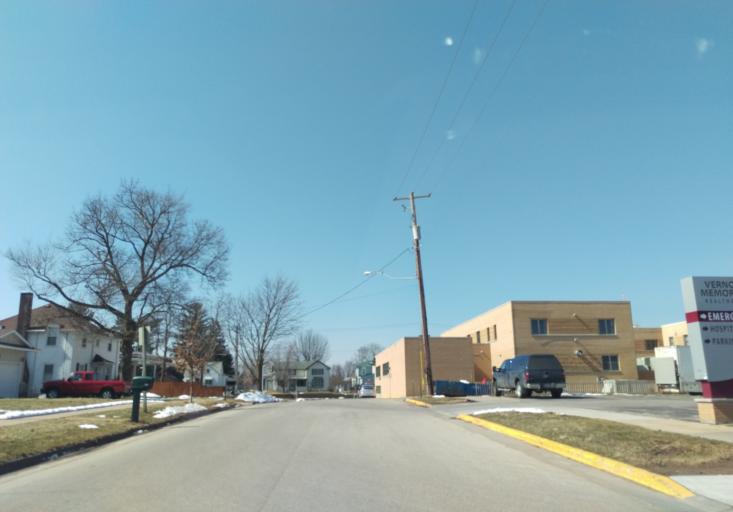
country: US
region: Wisconsin
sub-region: Vernon County
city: Viroqua
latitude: 43.5510
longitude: -90.8874
